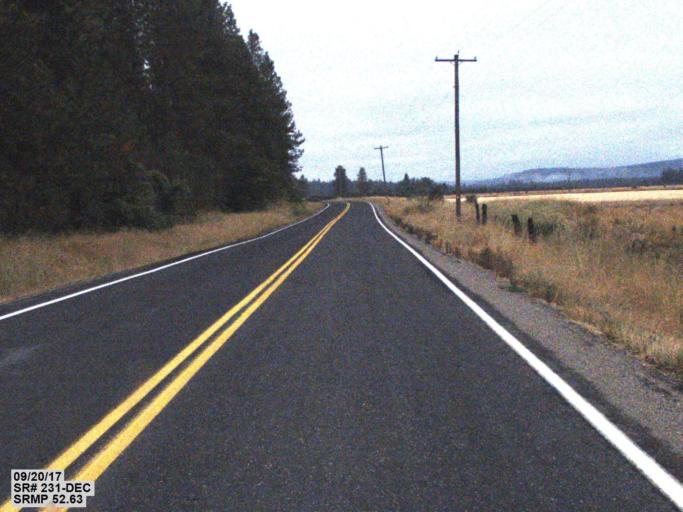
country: US
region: Washington
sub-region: Spokane County
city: Deer Park
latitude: 47.9314
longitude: -117.7736
